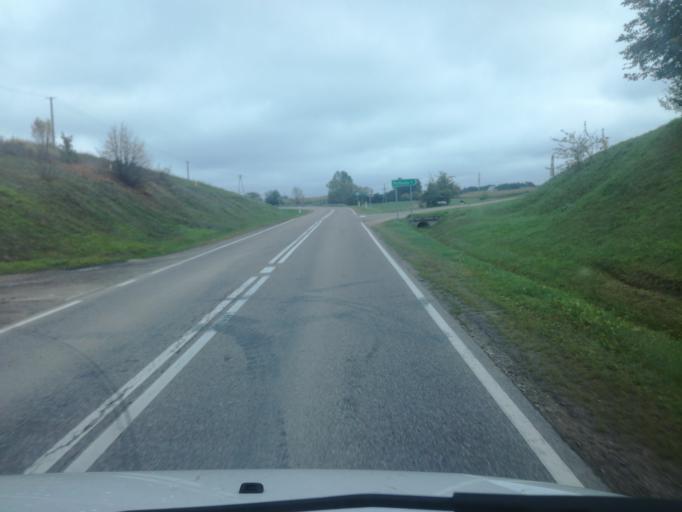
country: PL
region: Podlasie
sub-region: Powiat sejnenski
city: Sejny
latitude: 54.1158
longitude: 23.4259
